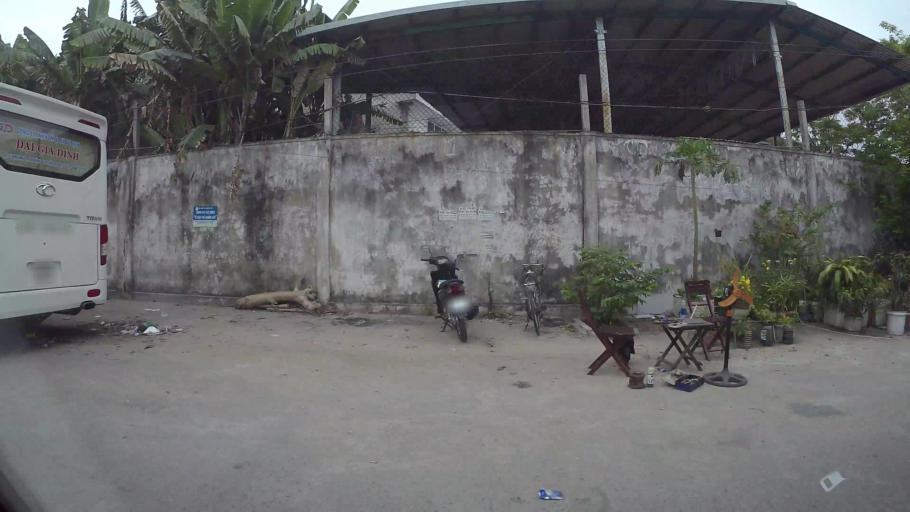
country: VN
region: Da Nang
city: Thanh Khe
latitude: 16.0679
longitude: 108.1777
